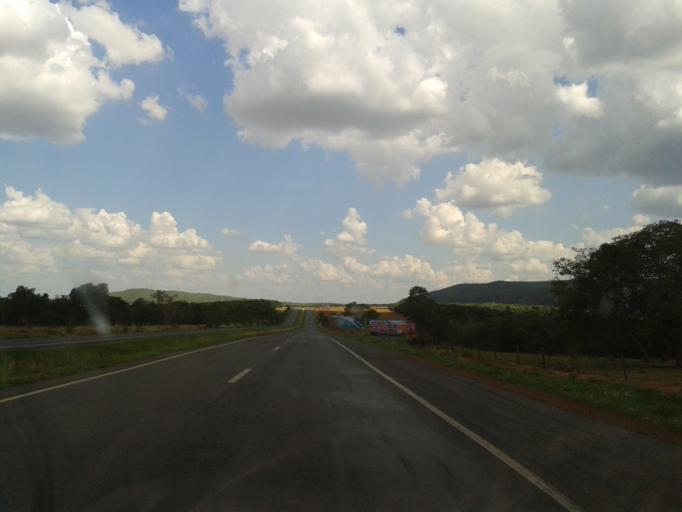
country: BR
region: Goias
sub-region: Caldas Novas
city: Caldas Novas
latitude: -17.7042
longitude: -48.7045
